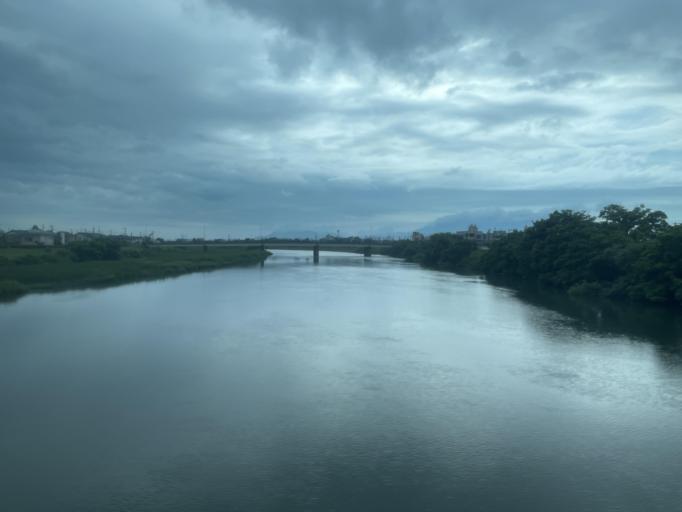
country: JP
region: Niigata
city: Tsubame
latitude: 37.6625
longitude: 138.9331
